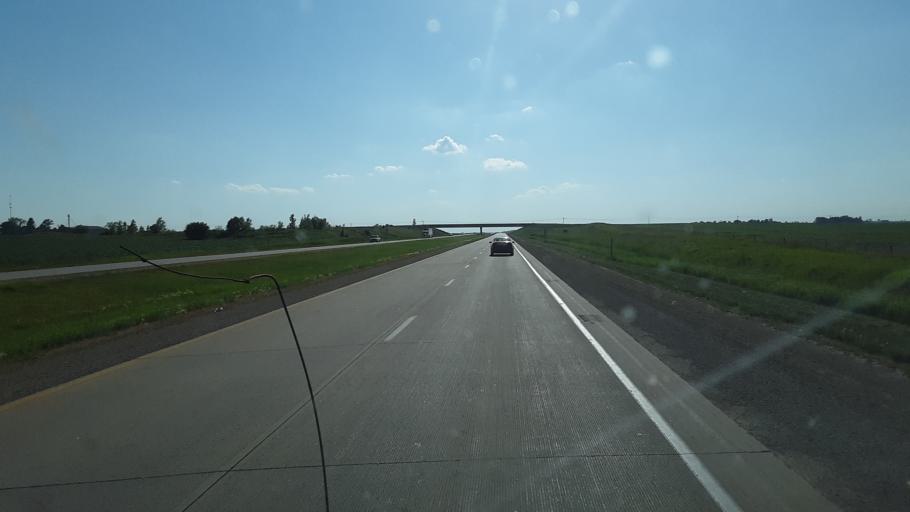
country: US
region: Iowa
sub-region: Grundy County
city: Dike
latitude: 42.4638
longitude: -92.6649
